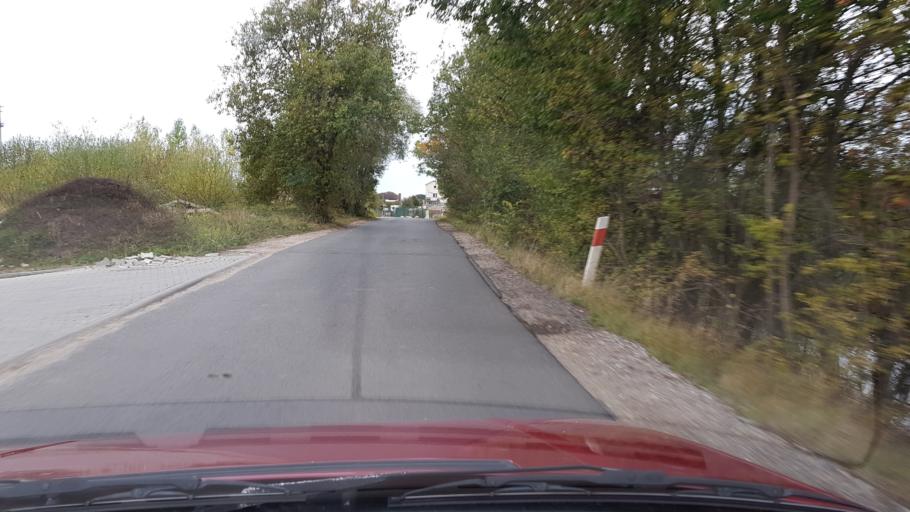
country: PL
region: West Pomeranian Voivodeship
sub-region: Koszalin
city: Koszalin
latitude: 54.1774
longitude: 16.1481
